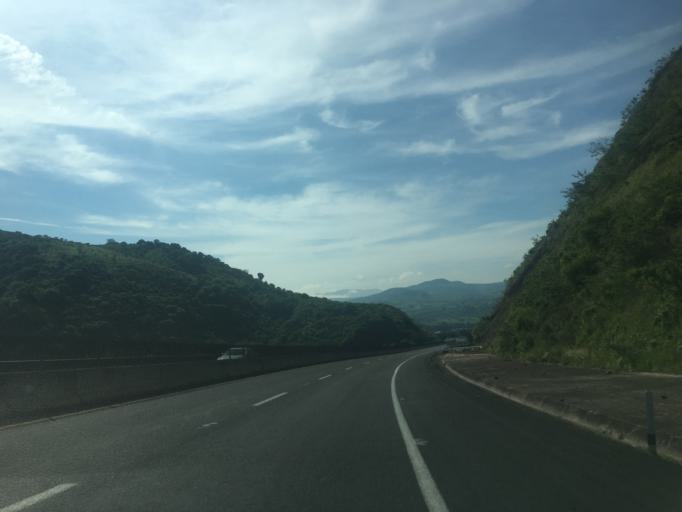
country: MX
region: Nayarit
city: Ixtlan del Rio
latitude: 21.0452
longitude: -104.3936
